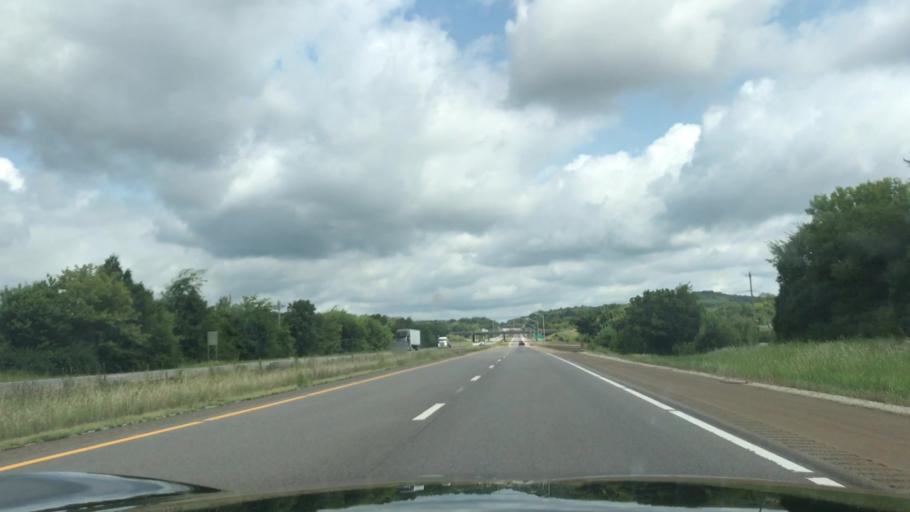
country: US
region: Kentucky
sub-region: Warren County
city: Bowling Green
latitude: 36.9868
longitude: -86.5026
